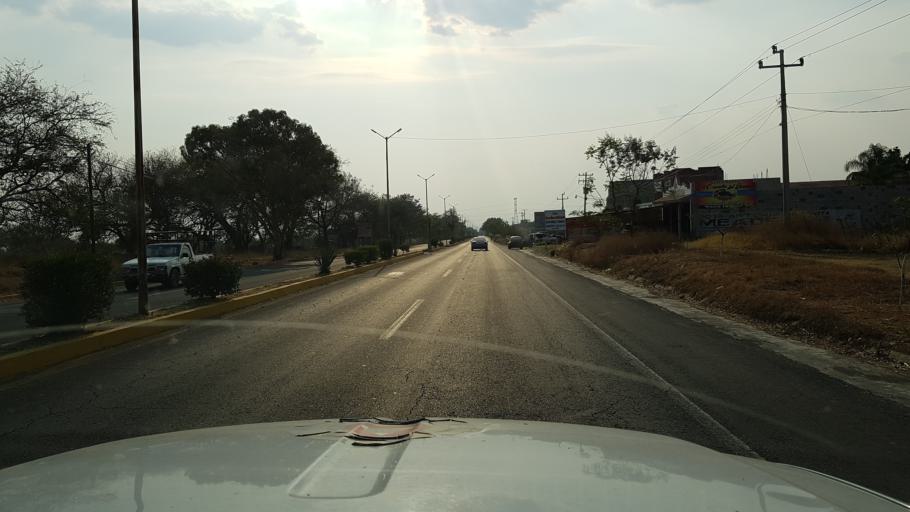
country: MX
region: Morelos
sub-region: Yecapixtla
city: Yecapixtla
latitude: 18.8894
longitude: -98.8788
